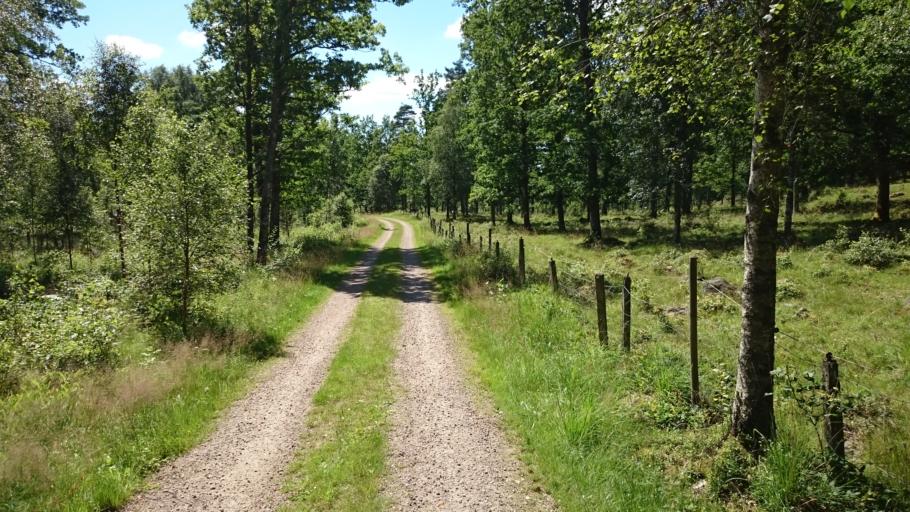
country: SE
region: Halland
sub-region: Hylte Kommun
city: Hyltebruk
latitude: 56.9755
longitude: 13.1687
